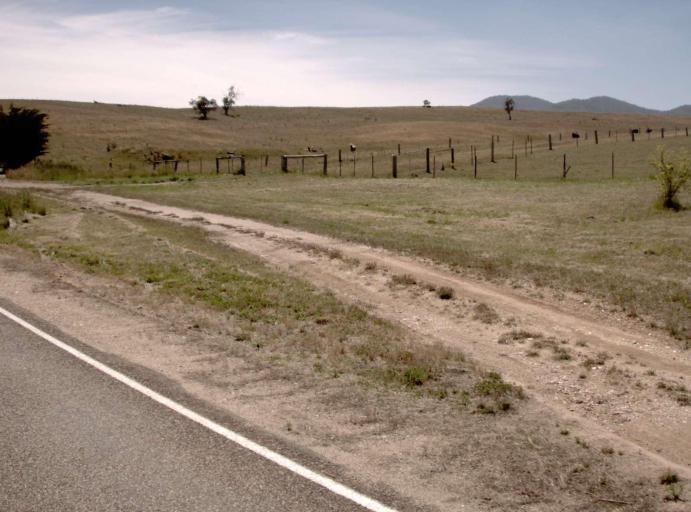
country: AU
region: Victoria
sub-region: Alpine
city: Mount Beauty
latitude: -37.0099
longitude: 147.6582
